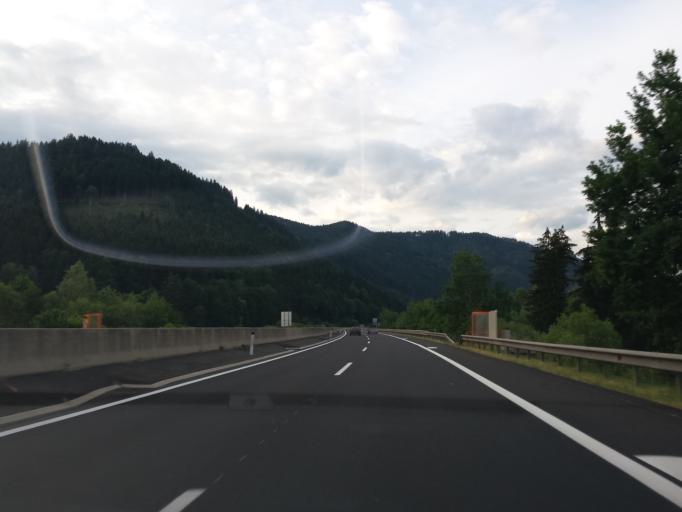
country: AT
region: Styria
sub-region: Politischer Bezirk Murtal
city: Feistritz bei Knittelfeld
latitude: 47.2667
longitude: 14.9109
